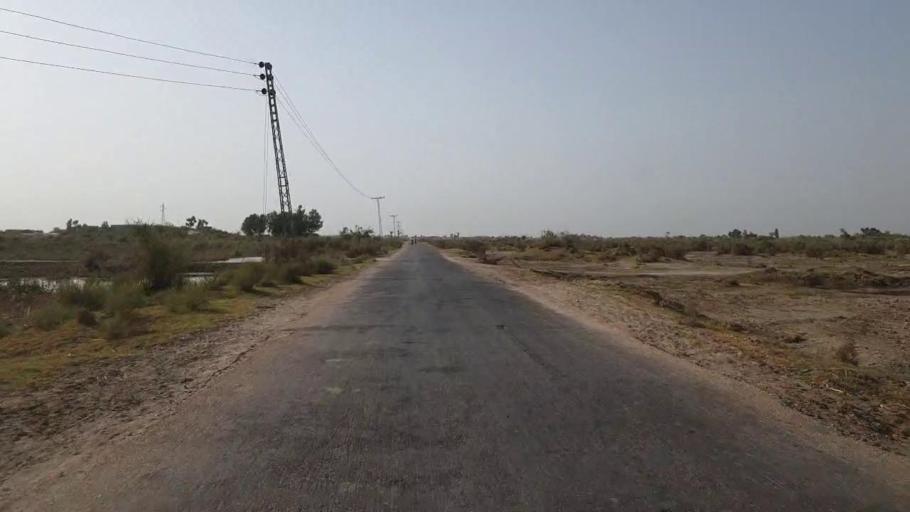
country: PK
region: Sindh
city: Khadro
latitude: 26.3440
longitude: 68.9251
